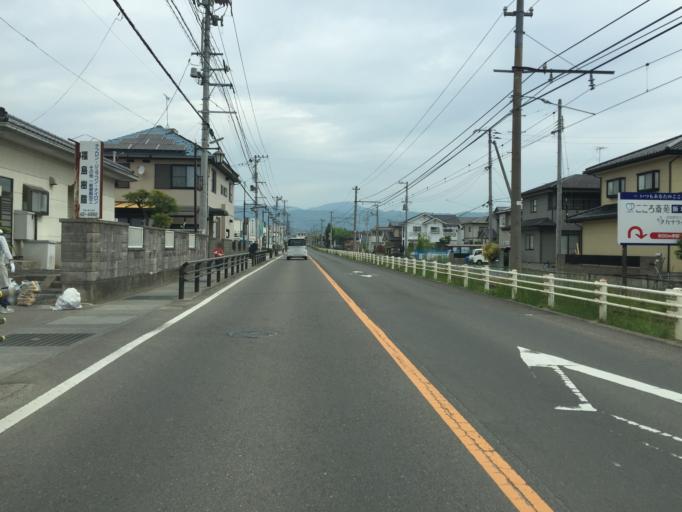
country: JP
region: Fukushima
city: Fukushima-shi
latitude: 37.8072
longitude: 140.4432
